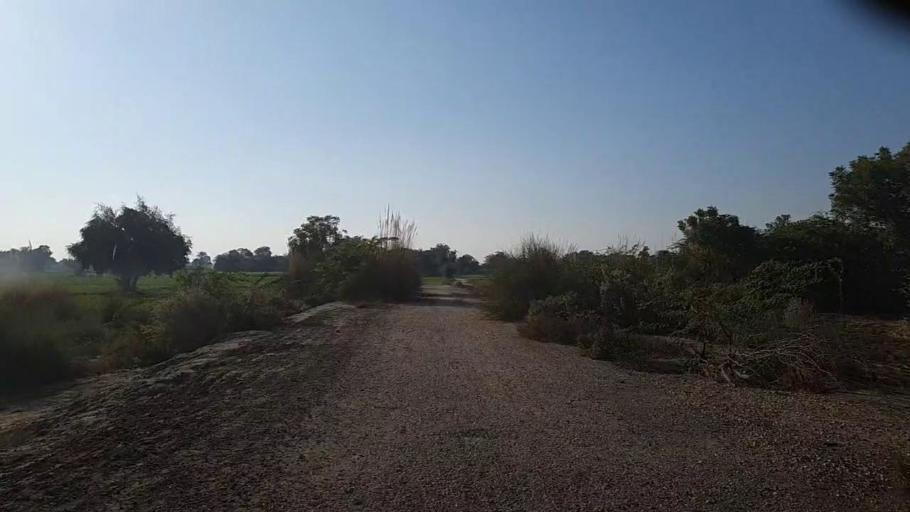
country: PK
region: Sindh
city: Darya Khan Marri
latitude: 26.6884
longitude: 68.3623
